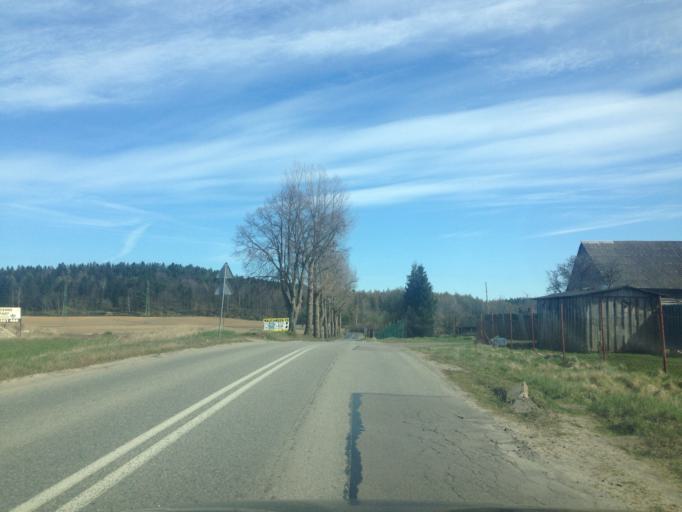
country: PL
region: Pomeranian Voivodeship
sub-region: Powiat kartuski
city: Chwaszczyno
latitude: 54.4818
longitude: 18.4385
